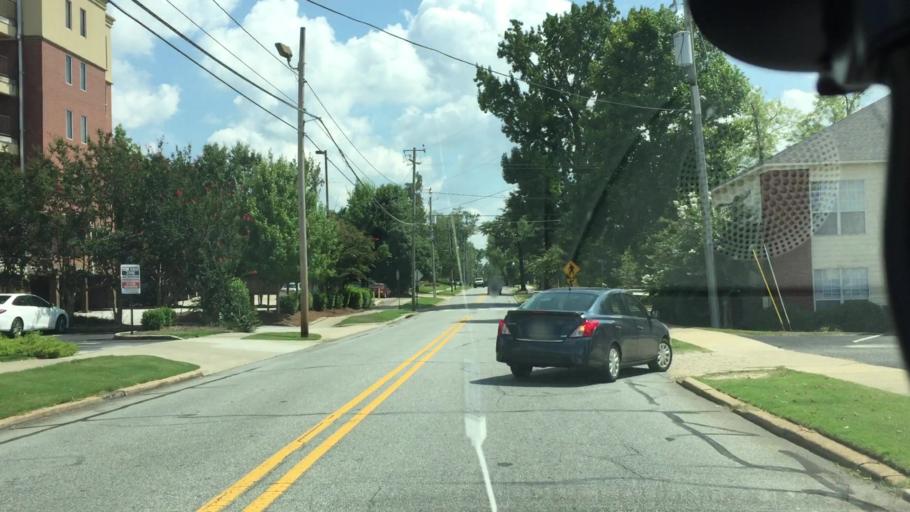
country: US
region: Alabama
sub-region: Lee County
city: Auburn
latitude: 32.6018
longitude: -85.4799
